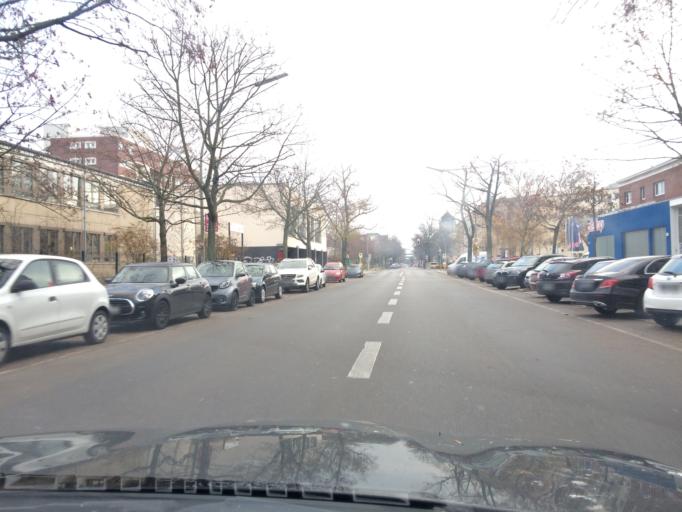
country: DE
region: Berlin
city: Moabit
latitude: 52.5304
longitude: 13.3523
